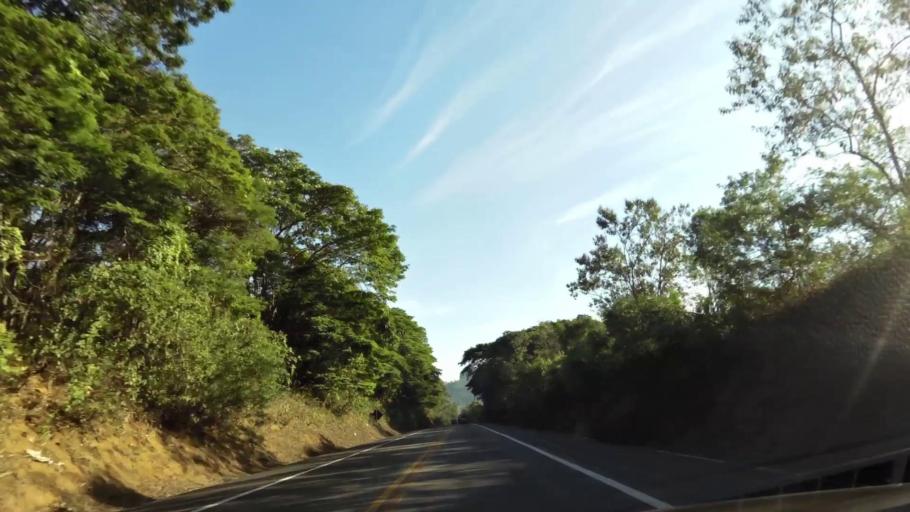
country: BR
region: Espirito Santo
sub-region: Guarapari
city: Guarapari
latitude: -20.5482
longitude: -40.4813
